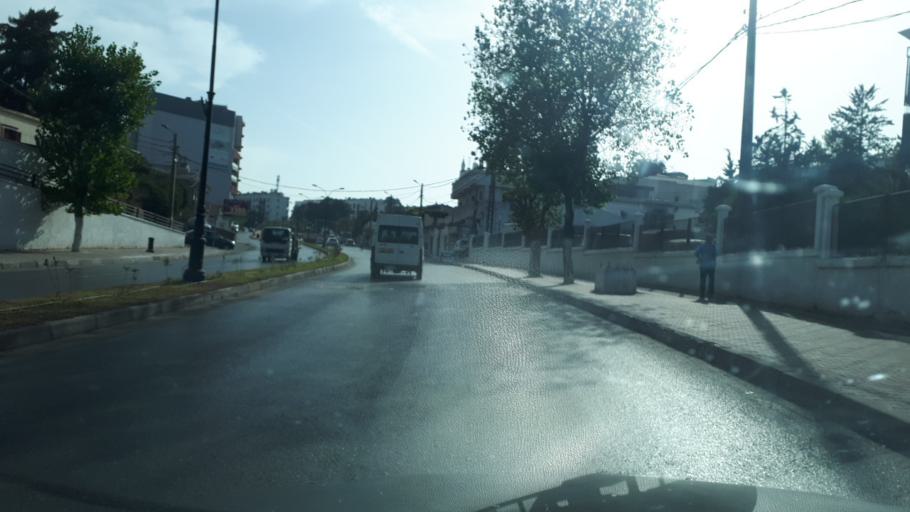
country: DZ
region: Alger
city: Algiers
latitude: 36.7705
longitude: 3.0129
